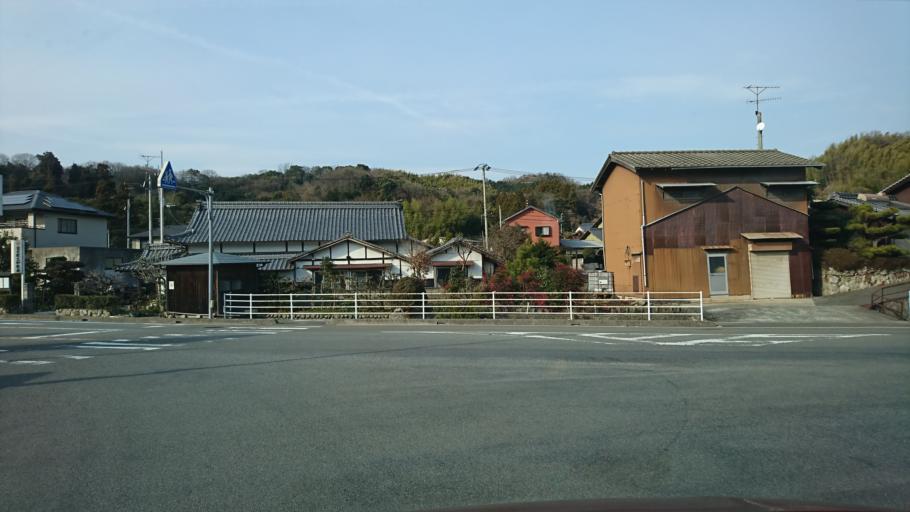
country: JP
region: Ehime
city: Hojo
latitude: 34.0273
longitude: 132.9597
